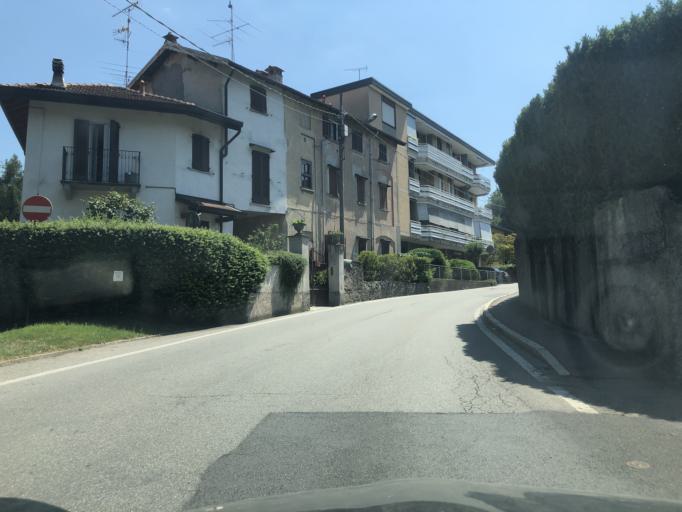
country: IT
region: Piedmont
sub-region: Provincia di Novara
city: Arona
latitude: 45.7511
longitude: 8.5487
